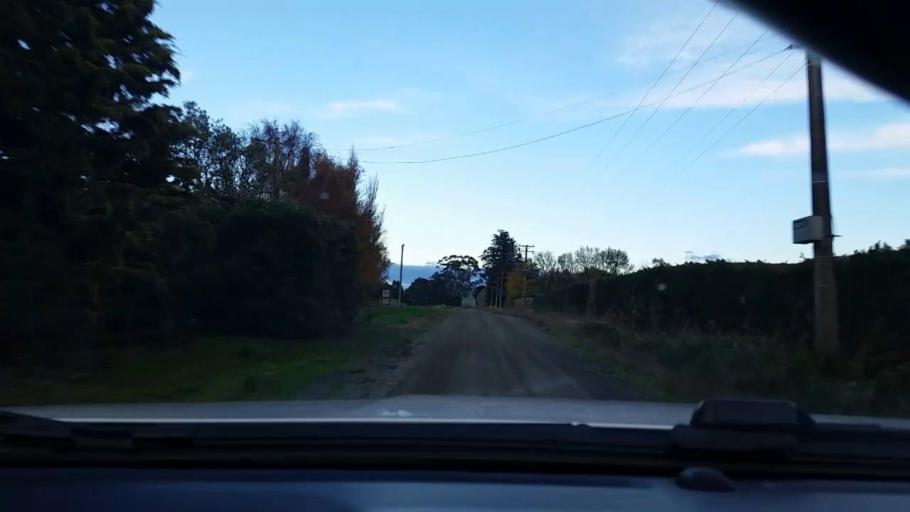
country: NZ
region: Southland
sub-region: Southland District
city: Winton
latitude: -46.1034
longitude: 168.4619
